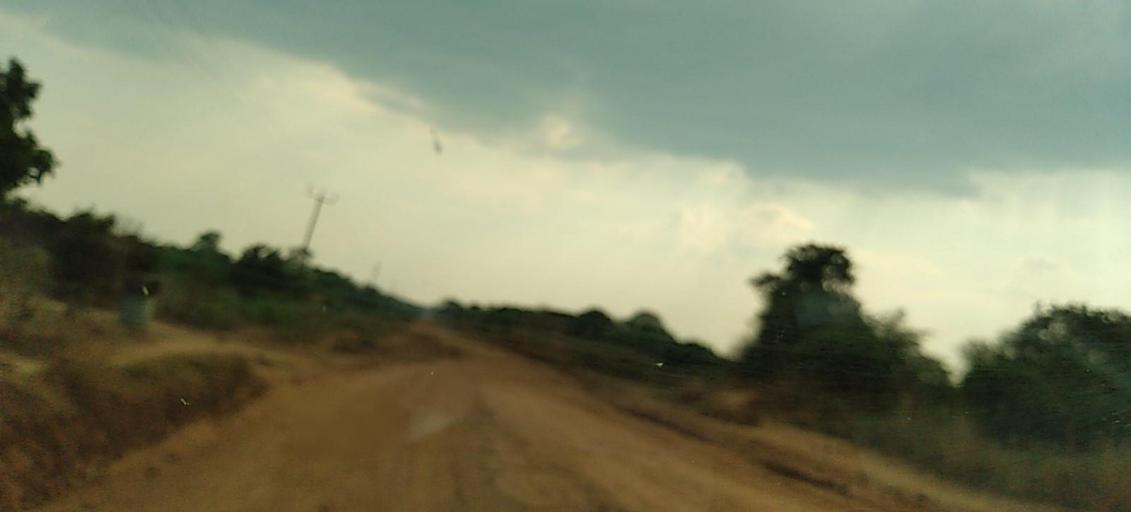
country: ZM
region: Copperbelt
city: Kalulushi
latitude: -12.9481
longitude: 27.9134
